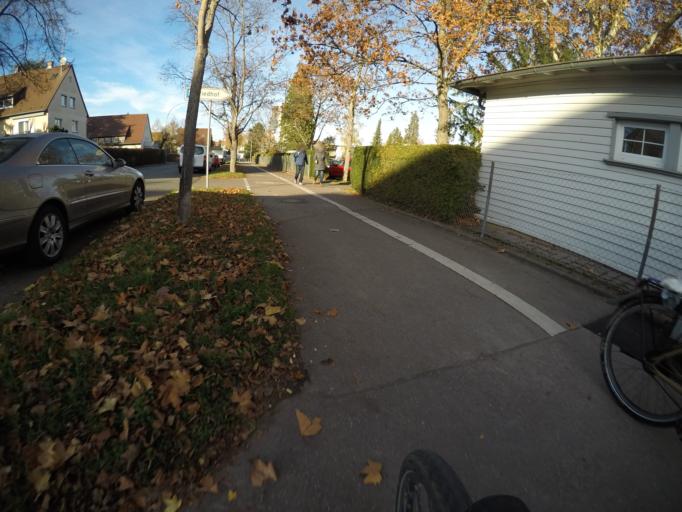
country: DE
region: Baden-Wuerttemberg
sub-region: Regierungsbezirk Stuttgart
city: Fellbach
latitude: 48.8101
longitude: 9.2823
